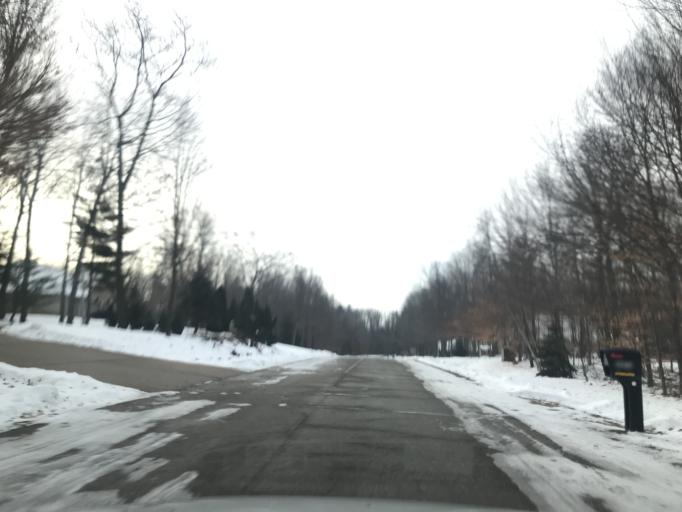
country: US
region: Wisconsin
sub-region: Brown County
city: Suamico
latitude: 44.6882
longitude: -88.0594
